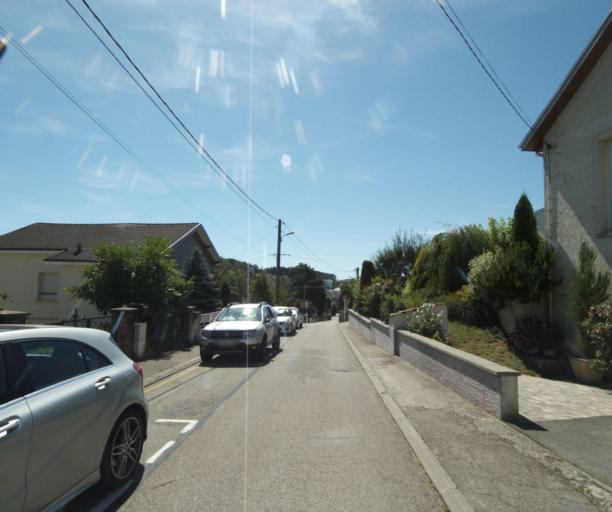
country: FR
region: Lorraine
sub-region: Departement des Vosges
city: Epinal
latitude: 48.1945
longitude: 6.4544
